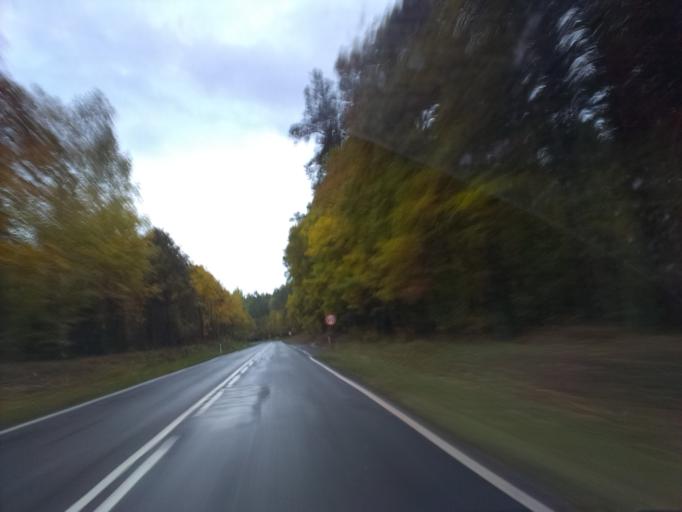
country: PL
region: Kujawsko-Pomorskie
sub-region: Powiat tucholski
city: Tuchola
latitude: 53.5577
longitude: 17.9015
